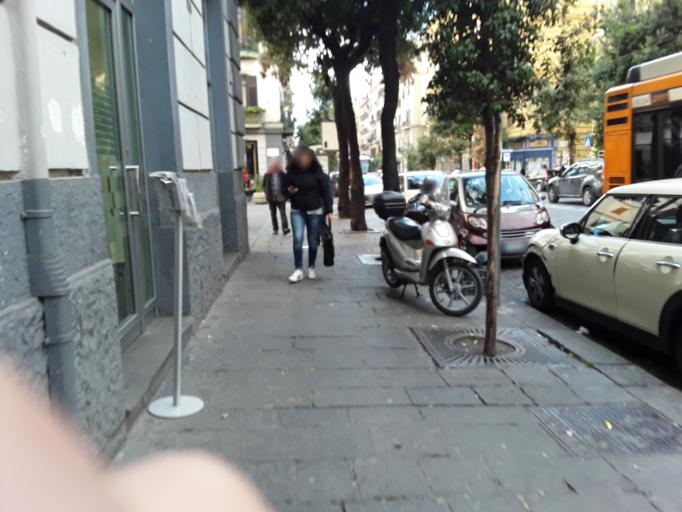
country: IT
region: Campania
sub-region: Provincia di Napoli
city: Napoli
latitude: 40.8612
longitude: 14.2666
